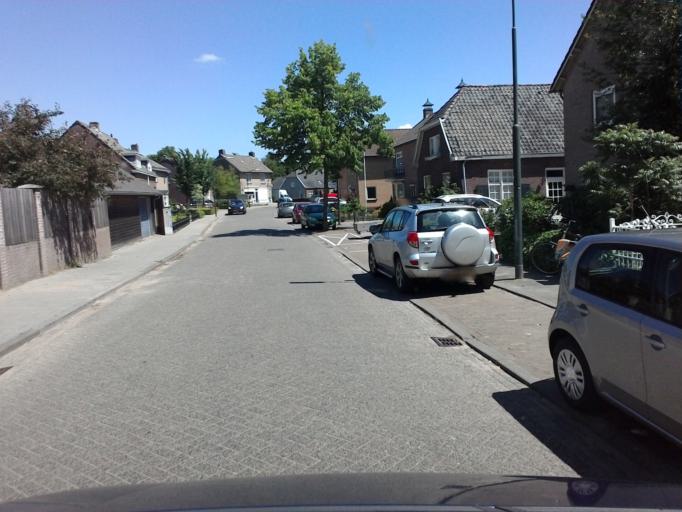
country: NL
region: North Brabant
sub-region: Gemeente Sint-Michielsgestel
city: Sint-Michielsgestel
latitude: 51.6394
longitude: 5.3520
